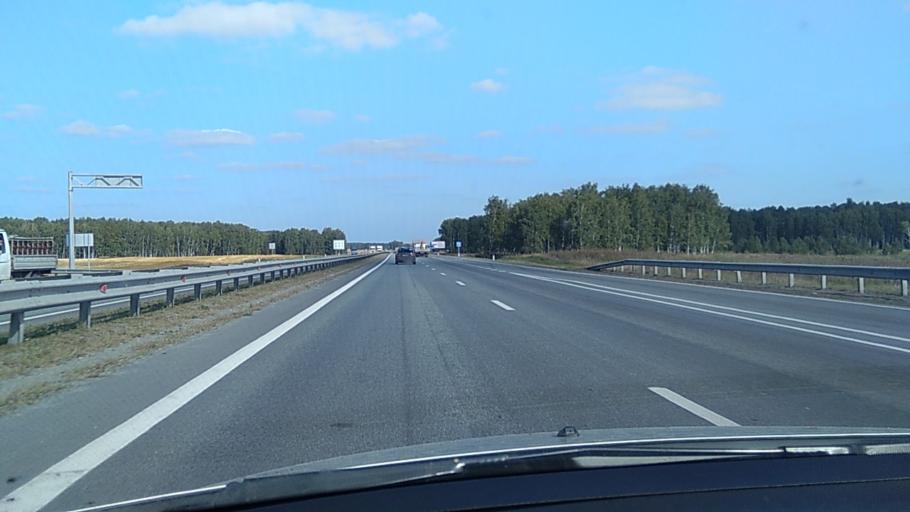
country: RU
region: Chelyabinsk
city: Timiryazevskiy
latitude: 54.9424
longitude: 60.8036
